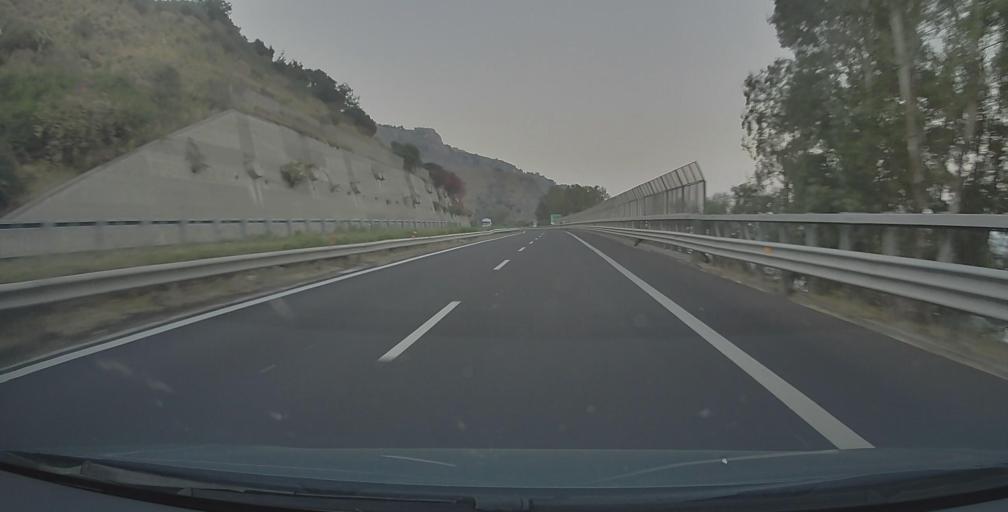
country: IT
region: Sicily
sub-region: Messina
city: Forza d'Agro
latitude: 37.8987
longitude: 15.3260
